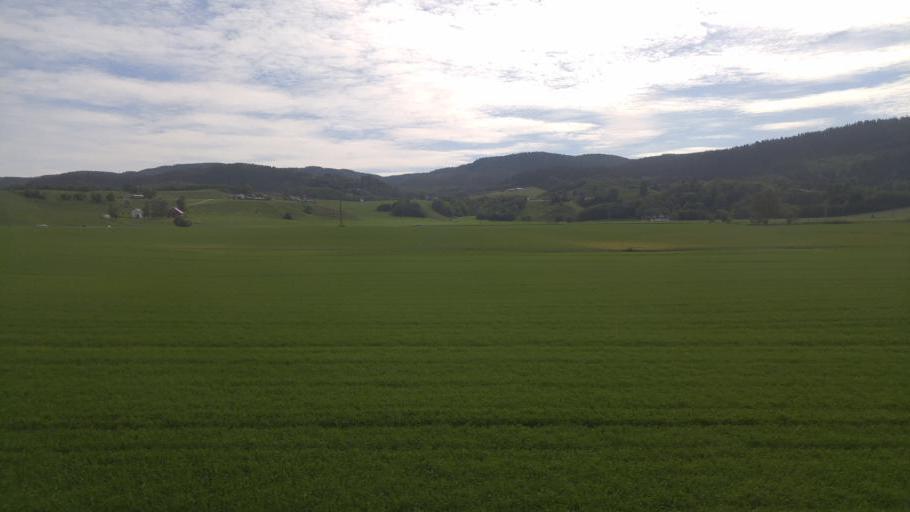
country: NO
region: Sor-Trondelag
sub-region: Melhus
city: Lundamo
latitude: 63.1810
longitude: 10.3080
